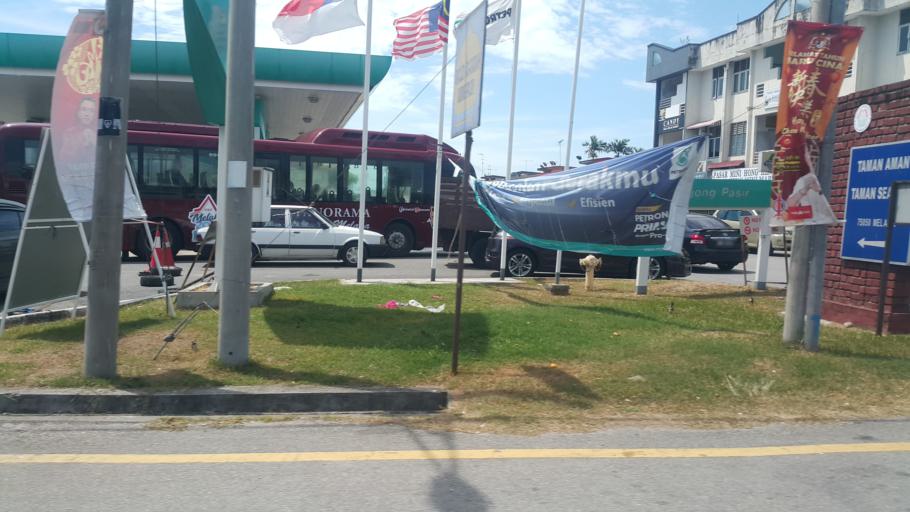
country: MY
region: Melaka
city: Kampung Bukit Baharu
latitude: 2.1871
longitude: 102.2710
